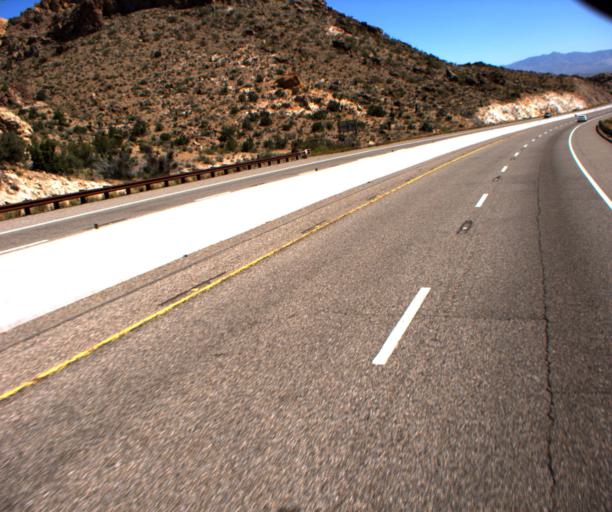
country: US
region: Arizona
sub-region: Mohave County
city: Golden Valley
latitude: 35.2226
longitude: -114.3865
